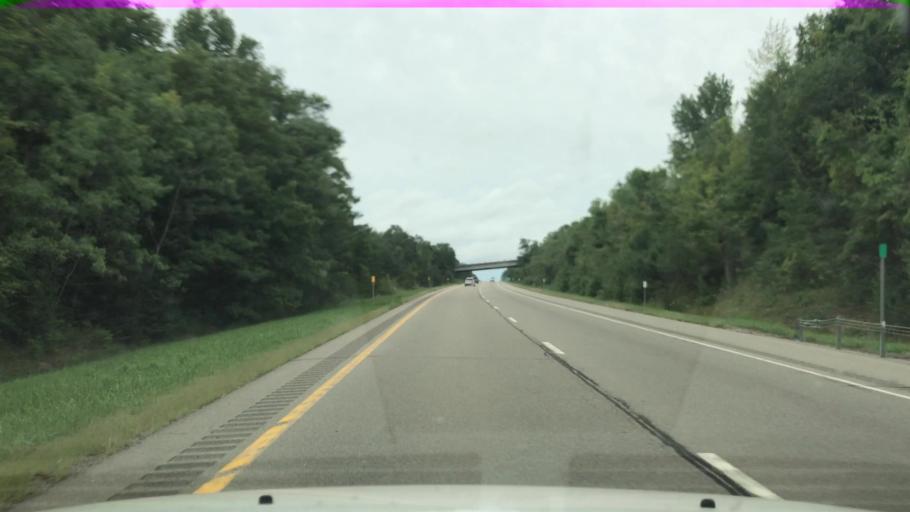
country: US
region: New York
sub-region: Erie County
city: North Boston
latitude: 42.6554
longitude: -78.7670
